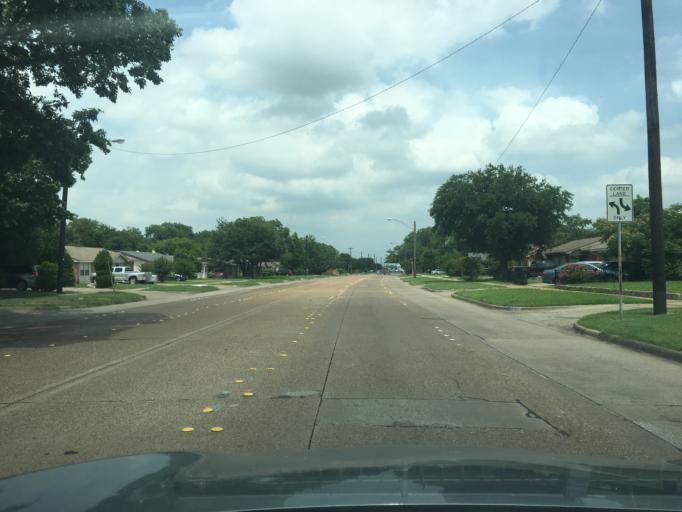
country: US
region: Texas
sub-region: Dallas County
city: Richardson
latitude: 32.9167
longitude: -96.6956
